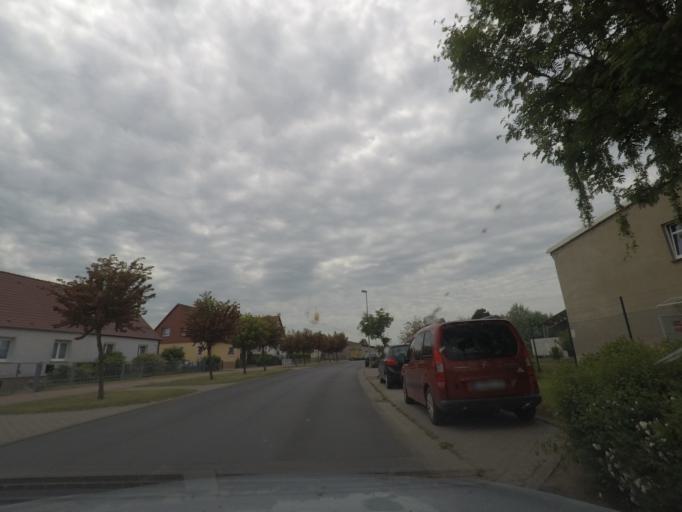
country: DE
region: Brandenburg
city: Prenzlau
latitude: 53.3265
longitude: 13.8724
